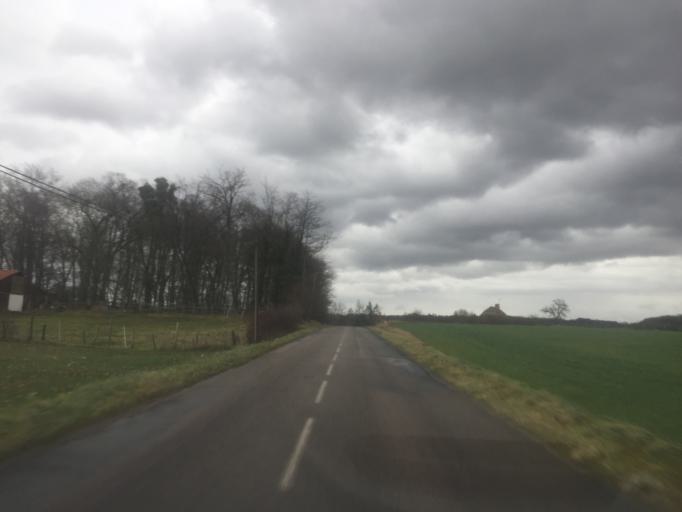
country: FR
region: Franche-Comte
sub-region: Departement de la Haute-Saone
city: Pesmes
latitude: 47.2191
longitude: 5.5106
